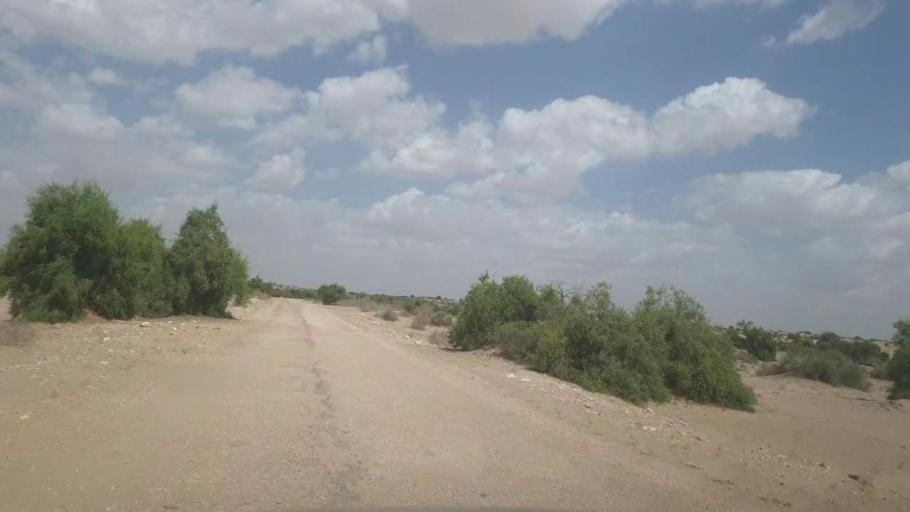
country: PK
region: Sindh
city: Kot Diji
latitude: 27.2712
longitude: 69.2050
